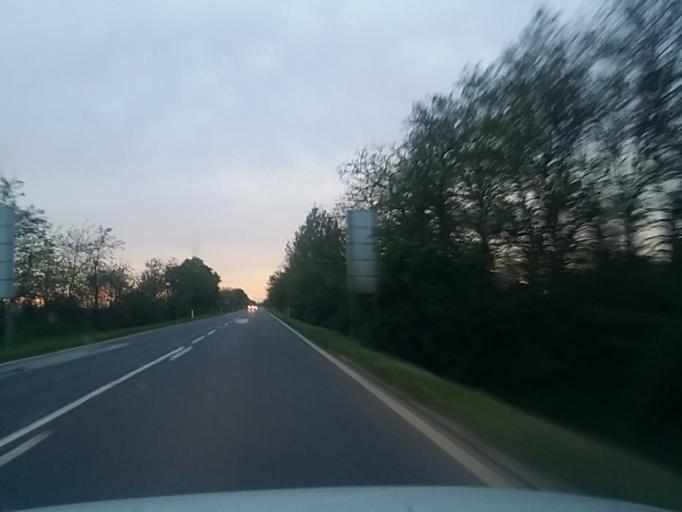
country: HU
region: Bekes
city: Csorvas
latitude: 46.7175
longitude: 20.9347
